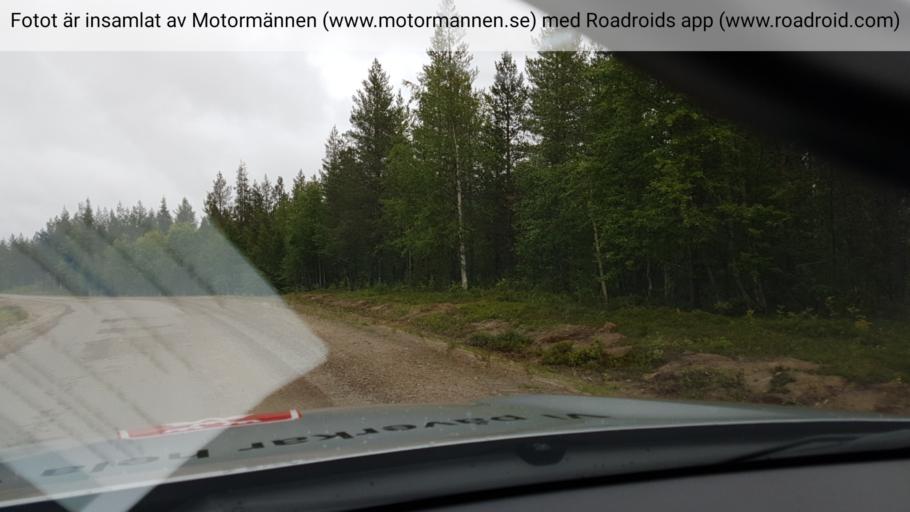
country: SE
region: Norrbotten
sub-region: Gallivare Kommun
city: Gaellivare
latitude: 66.7380
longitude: 20.8419
